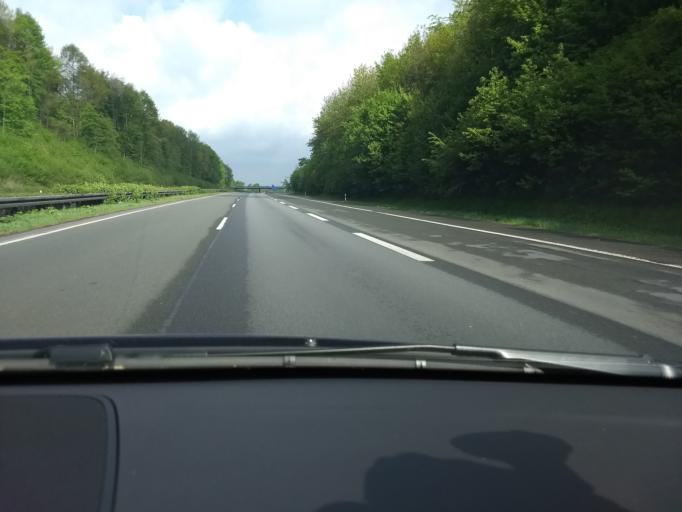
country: DE
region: North Rhine-Westphalia
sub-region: Regierungsbezirk Arnsberg
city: Werl
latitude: 51.5156
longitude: 7.9028
